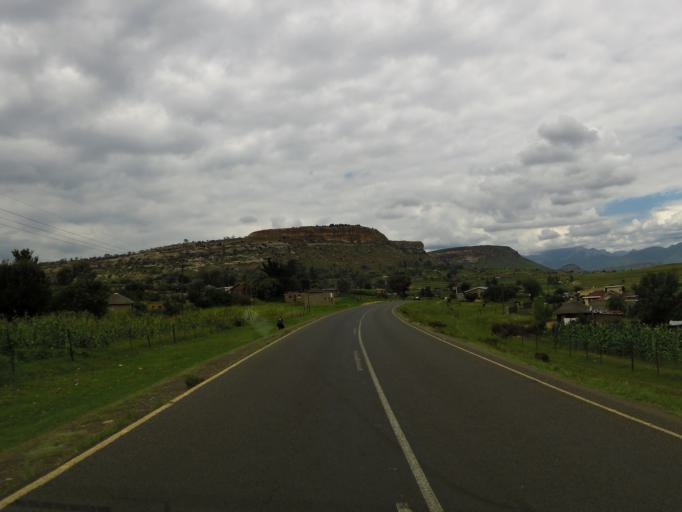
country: LS
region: Leribe
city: Leribe
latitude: -28.9374
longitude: 28.1666
